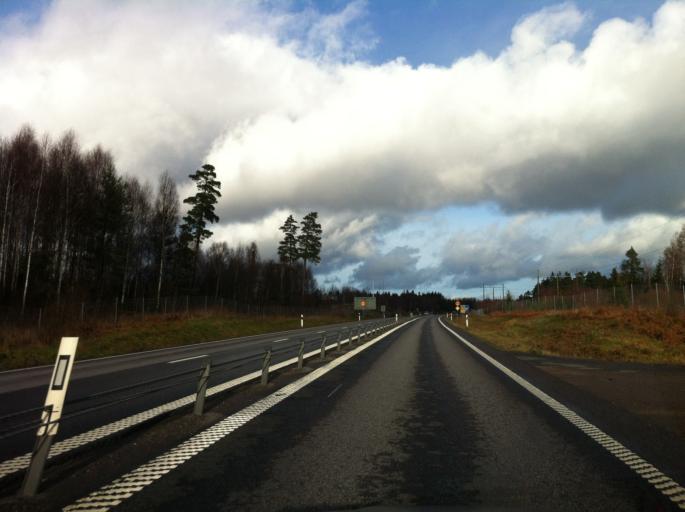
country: SE
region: Kronoberg
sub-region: Almhults Kommun
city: AElmhult
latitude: 56.5102
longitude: 14.1297
